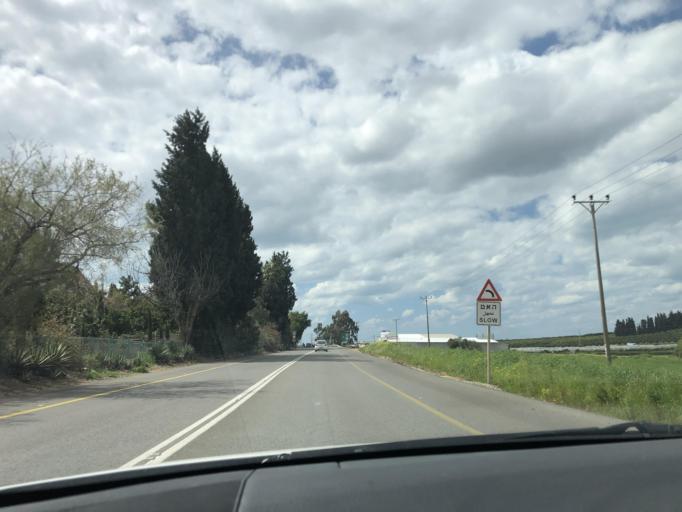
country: IL
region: Central District
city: Tel Mond
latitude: 32.2619
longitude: 34.9208
